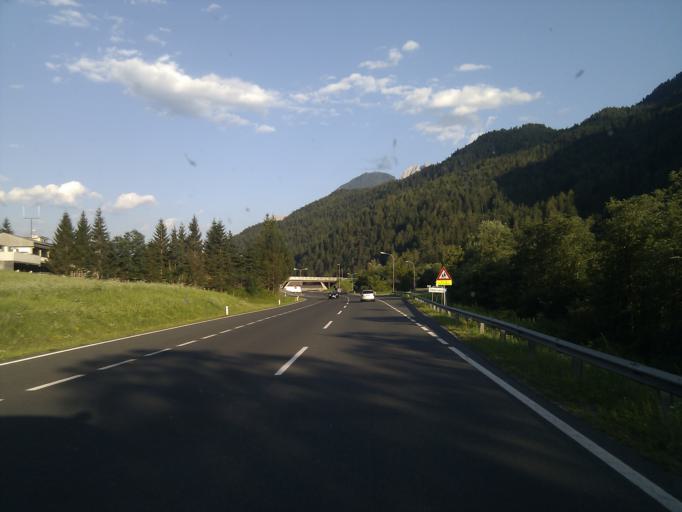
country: AT
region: Tyrol
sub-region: Politischer Bezirk Lienz
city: Oberlienz
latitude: 46.8411
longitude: 12.7226
